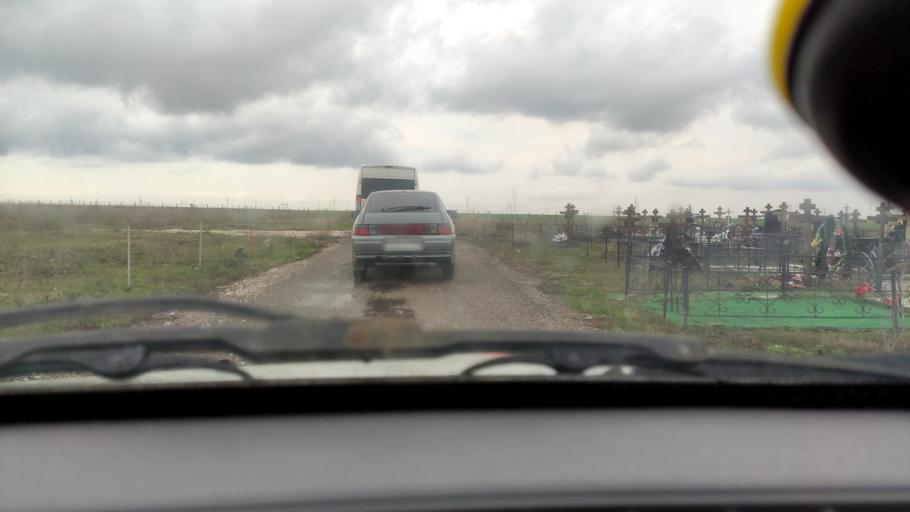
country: RU
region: Samara
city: Povolzhskiy
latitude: 53.6306
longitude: 49.6568
